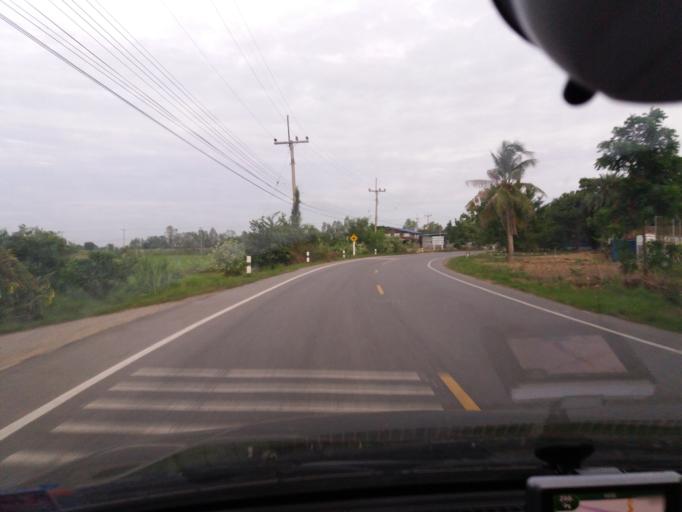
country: TH
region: Suphan Buri
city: Don Chedi
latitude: 14.7052
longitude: 100.0253
